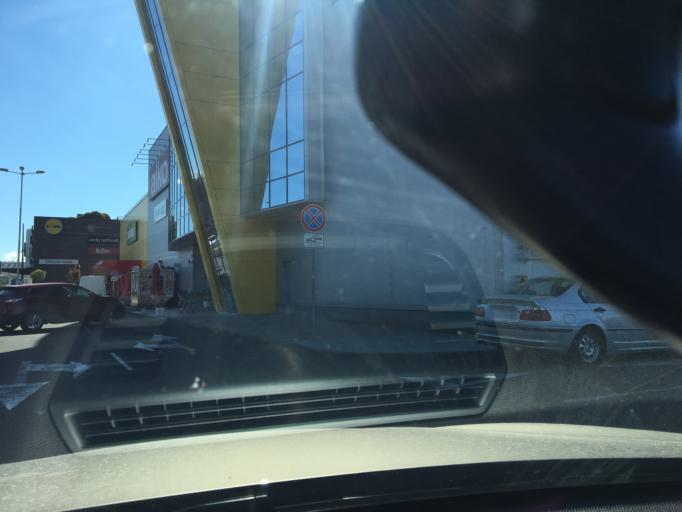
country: BG
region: Burgas
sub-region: Obshtina Burgas
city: Burgas
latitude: 42.5141
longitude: 27.4524
